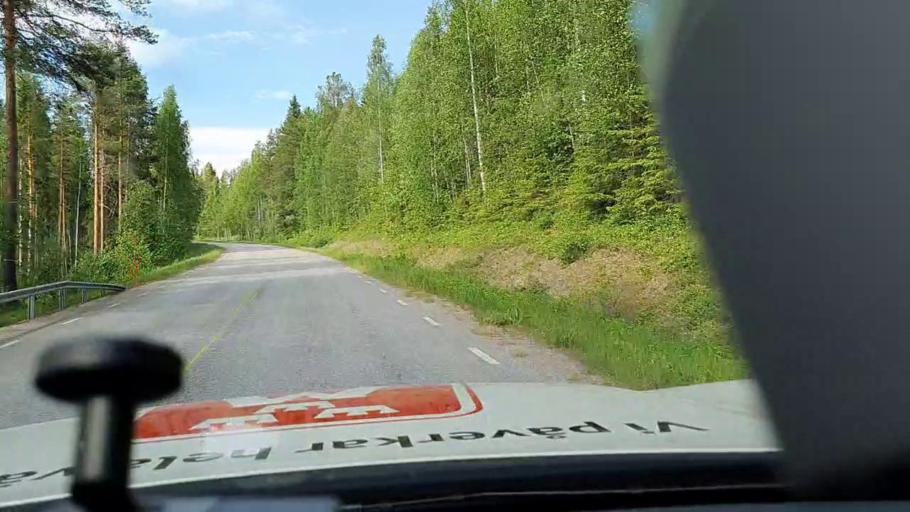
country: SE
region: Norrbotten
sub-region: Gallivare Kommun
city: Gaellivare
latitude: 66.4532
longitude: 20.6570
